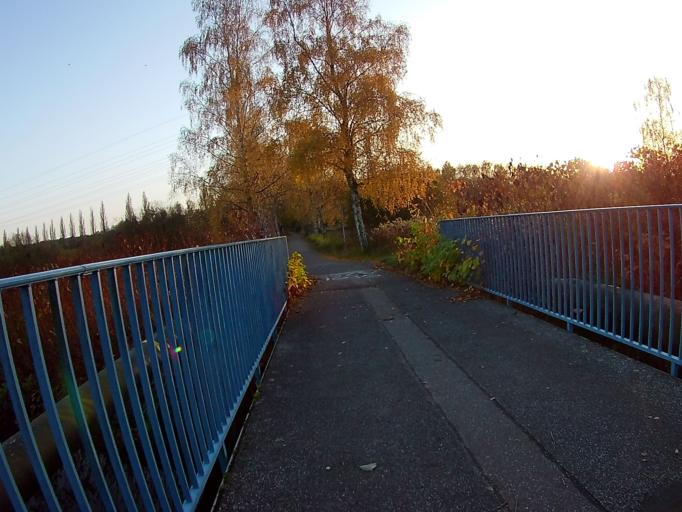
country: DE
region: Hamburg
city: Harburg
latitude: 53.4805
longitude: 9.9264
